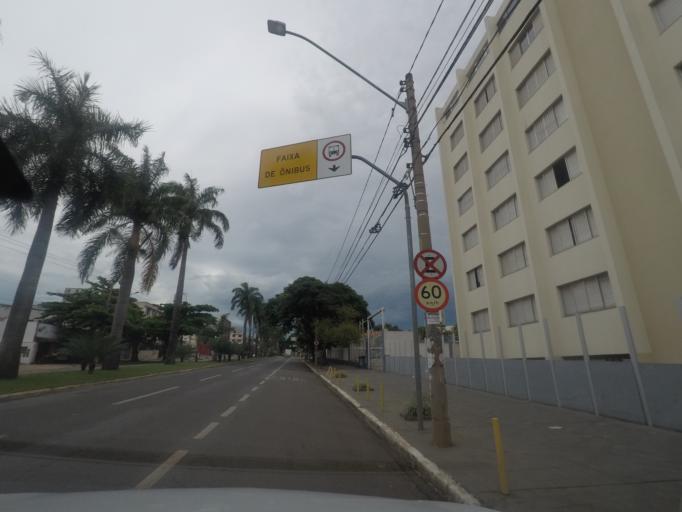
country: BR
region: Goias
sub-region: Goiania
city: Goiania
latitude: -16.6931
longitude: -49.2631
